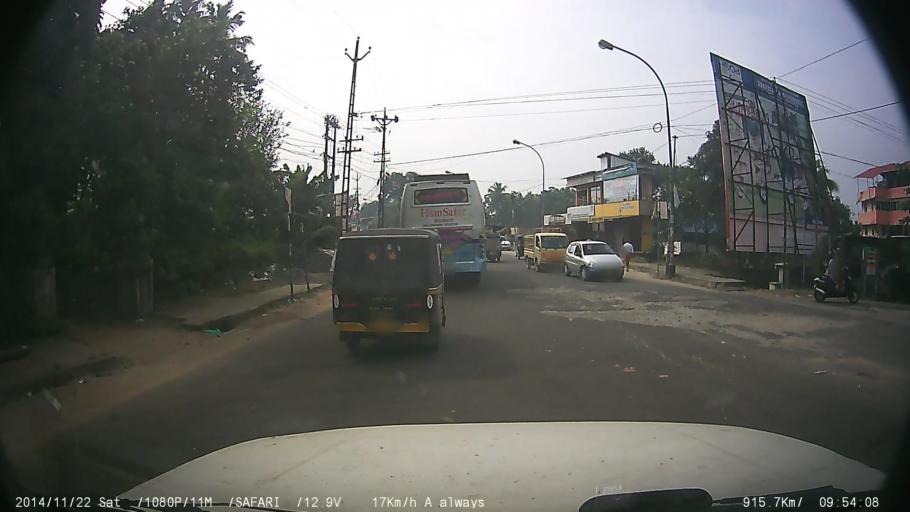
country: IN
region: Kerala
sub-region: Ernakulam
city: Perumpavur
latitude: 10.1118
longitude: 76.4792
